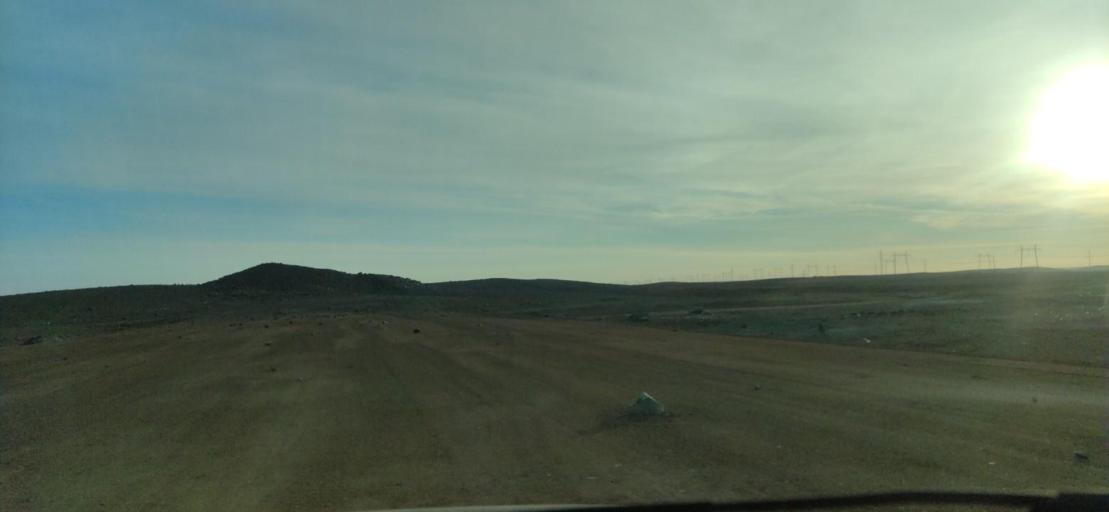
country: KZ
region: Qaraghandy
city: Saryshaghan
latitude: 46.1180
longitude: 73.5947
